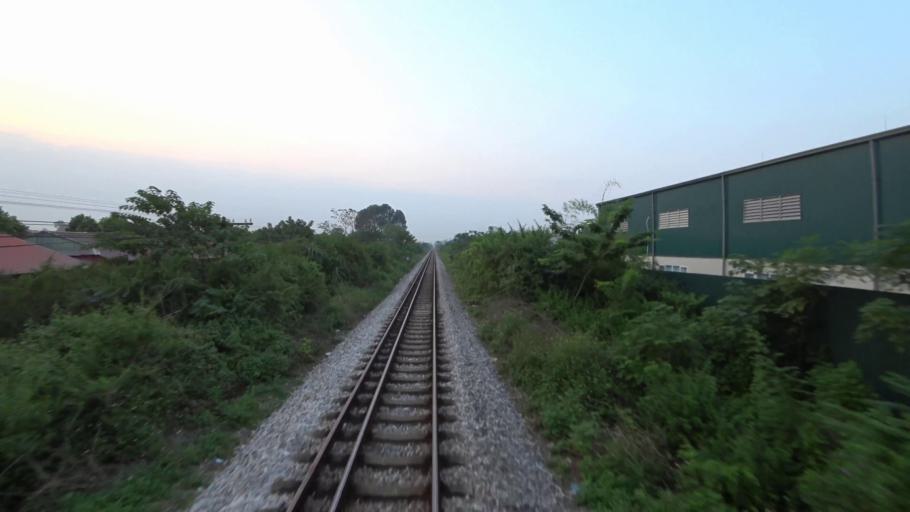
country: VN
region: Ha Noi
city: Dong Anh
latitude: 21.1445
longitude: 105.8619
